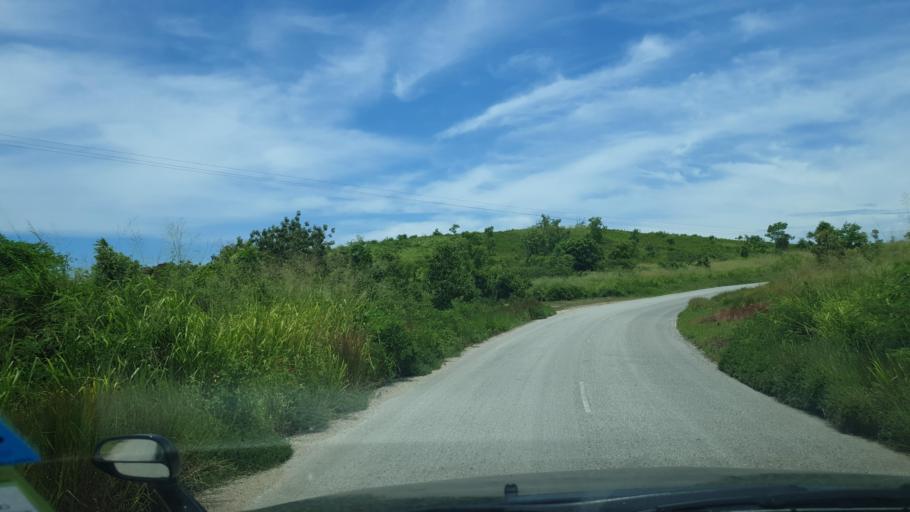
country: PG
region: National Capital
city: Port Moresby
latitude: -9.4306
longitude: 147.0552
